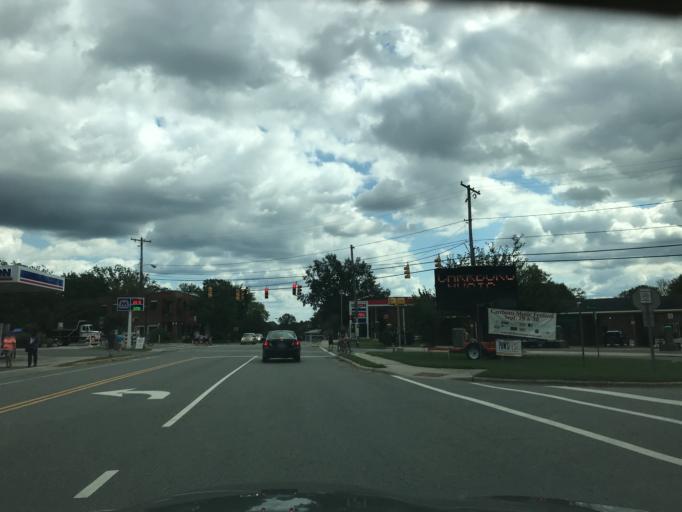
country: US
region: North Carolina
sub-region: Orange County
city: Carrboro
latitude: 35.9116
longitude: -79.0771
